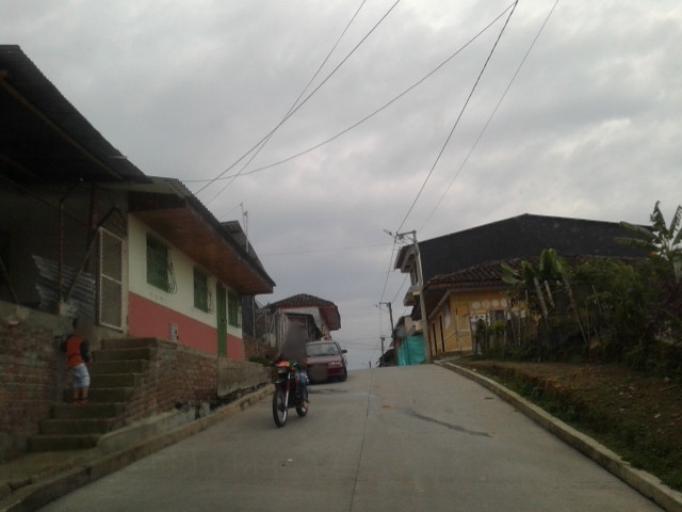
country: CO
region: Quindio
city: Filandia
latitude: 4.6736
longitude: -75.6607
